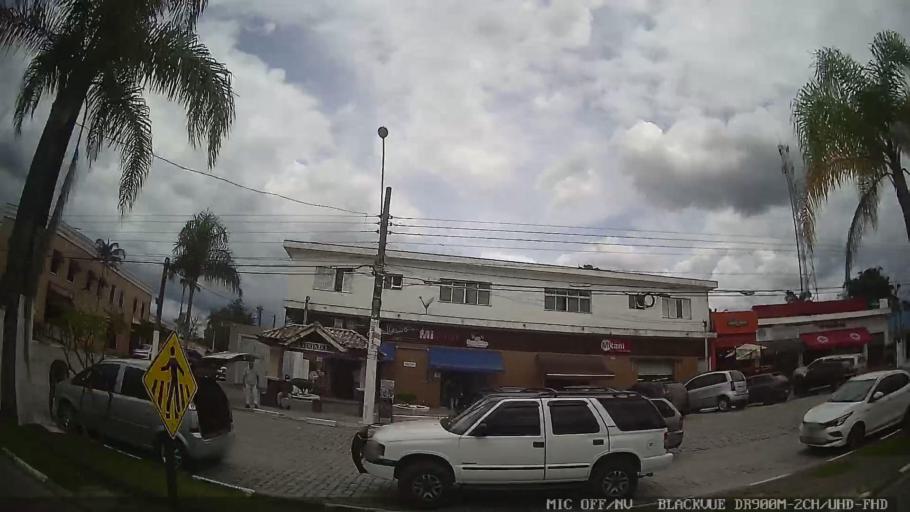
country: BR
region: Sao Paulo
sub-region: Ribeirao Pires
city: Ribeirao Pires
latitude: -23.6776
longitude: -46.3519
